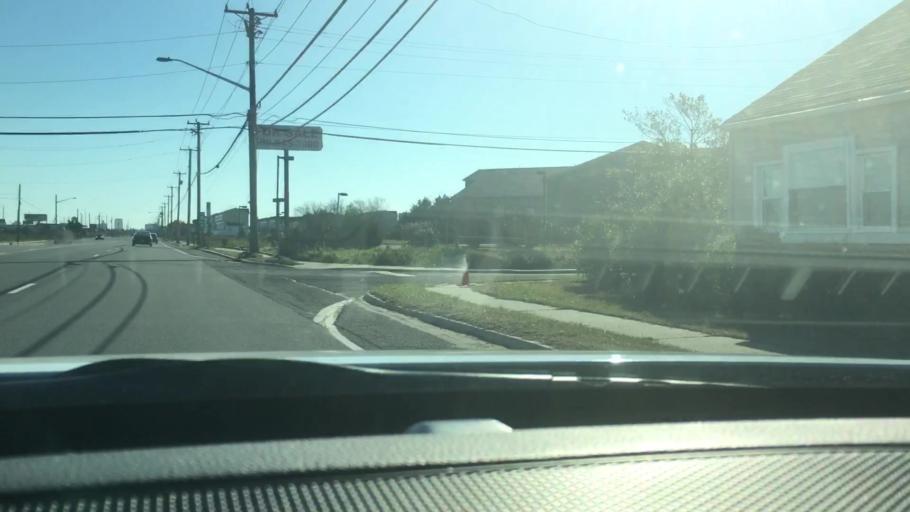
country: US
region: New Jersey
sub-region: Atlantic County
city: Pleasantville
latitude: 39.3822
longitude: -74.4994
